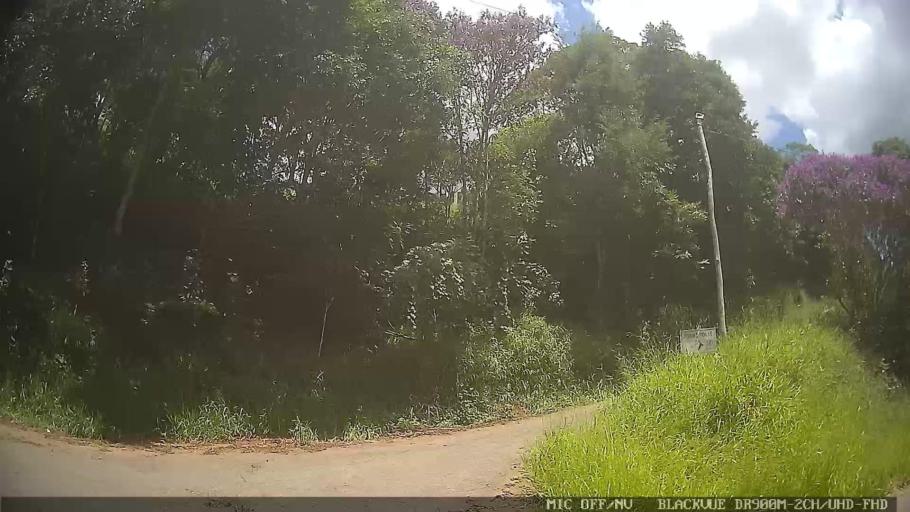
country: BR
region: Minas Gerais
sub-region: Extrema
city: Extrema
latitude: -22.8681
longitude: -46.2880
